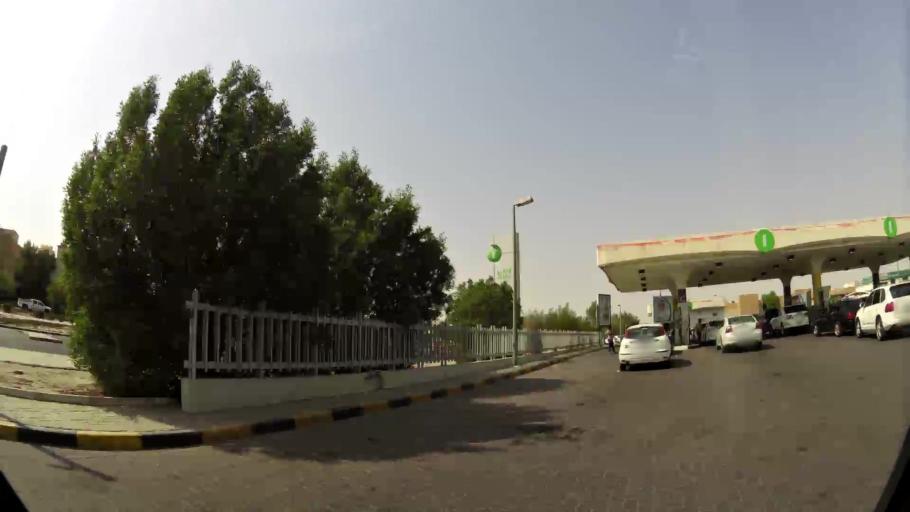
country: KW
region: Muhafazat al Jahra'
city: Al Jahra'
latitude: 29.3358
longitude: 47.6980
